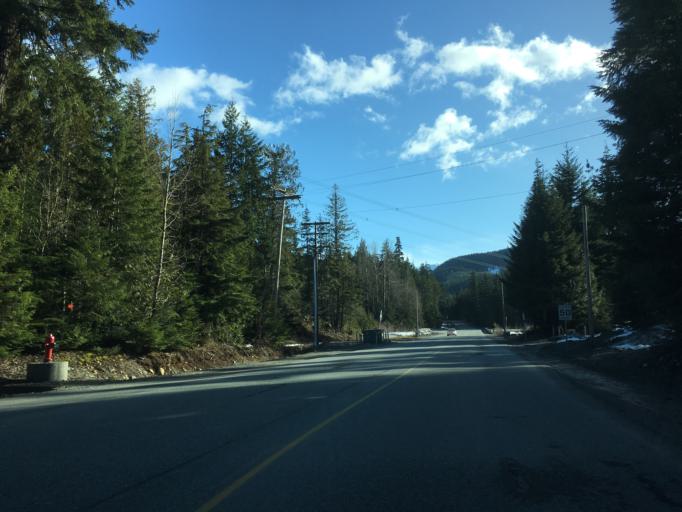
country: CA
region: British Columbia
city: Whistler
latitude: 50.0861
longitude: -123.0368
